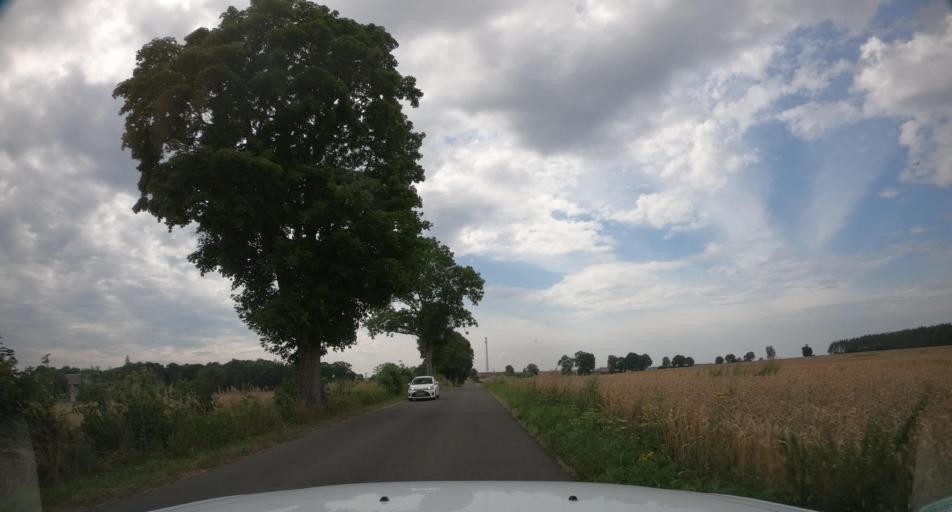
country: PL
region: West Pomeranian Voivodeship
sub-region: Powiat walecki
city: Walcz
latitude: 53.2341
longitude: 16.3198
